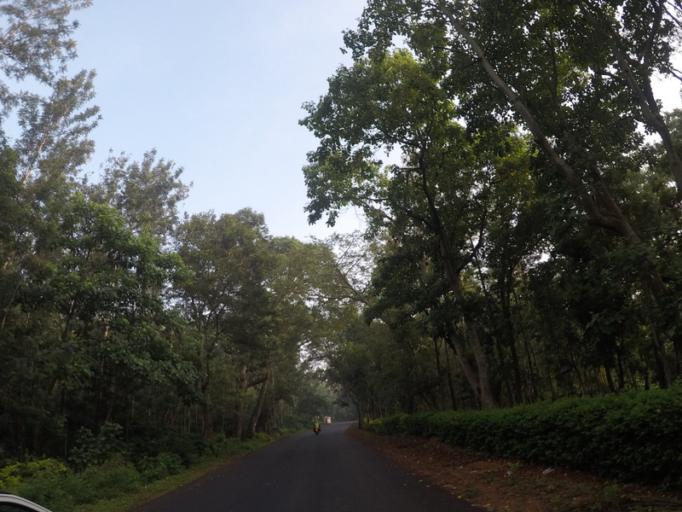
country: IN
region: Karnataka
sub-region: Chikmagalur
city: Chikmagalur
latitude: 13.4079
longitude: 75.7961
